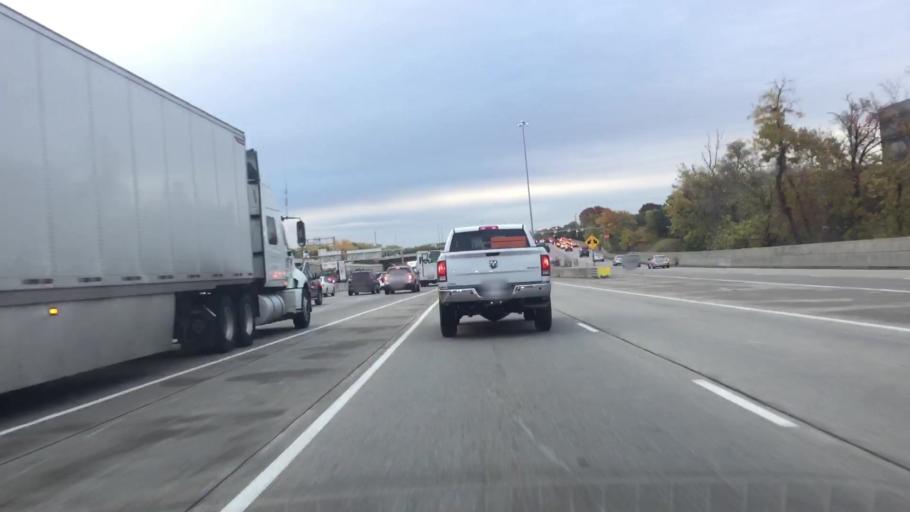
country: US
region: Kansas
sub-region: Johnson County
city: Lenexa
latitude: 38.9367
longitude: -94.6924
